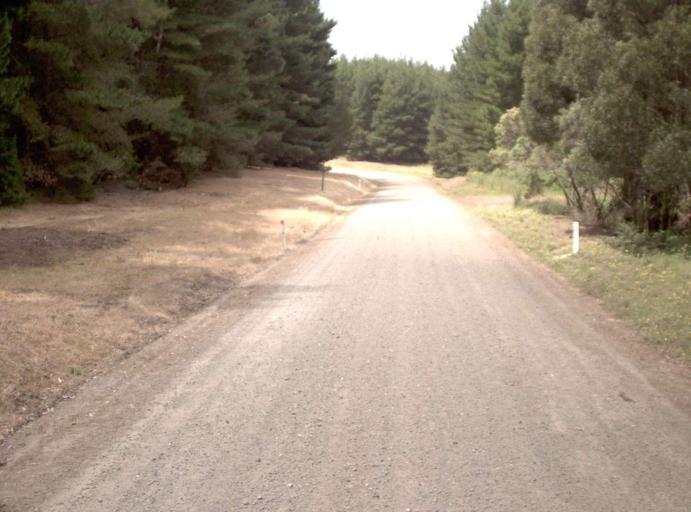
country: AU
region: Victoria
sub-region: Latrobe
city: Traralgon
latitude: -38.3851
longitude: 146.6638
